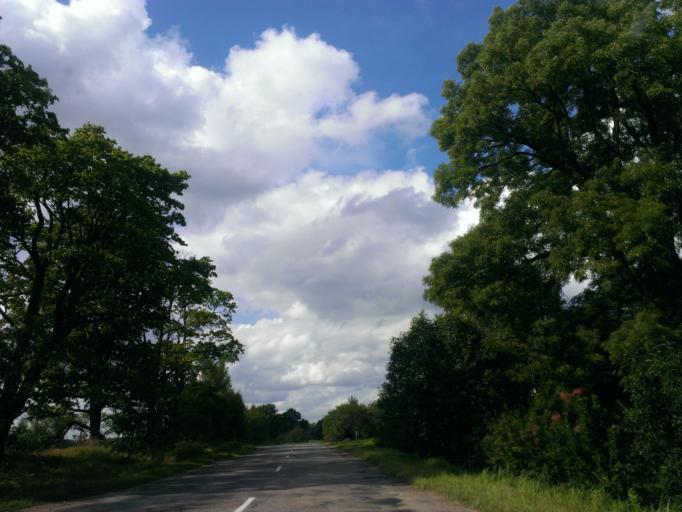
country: LV
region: Ropazu
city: Ropazi
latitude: 56.9641
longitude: 24.5278
